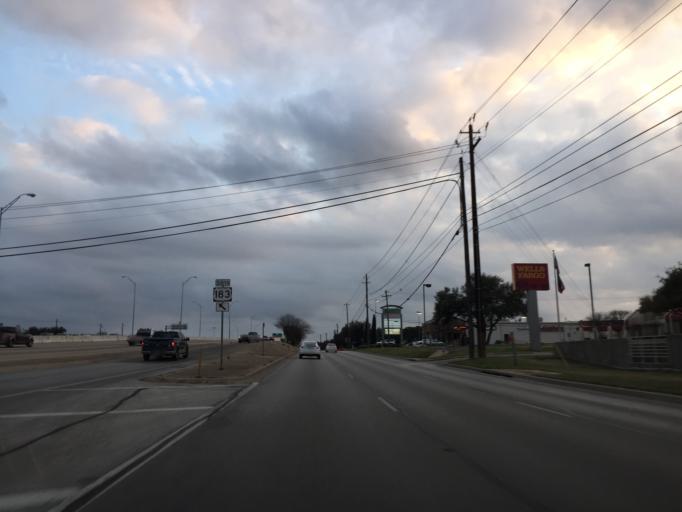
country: US
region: Texas
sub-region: Williamson County
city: Jollyville
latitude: 30.3974
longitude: -97.7466
